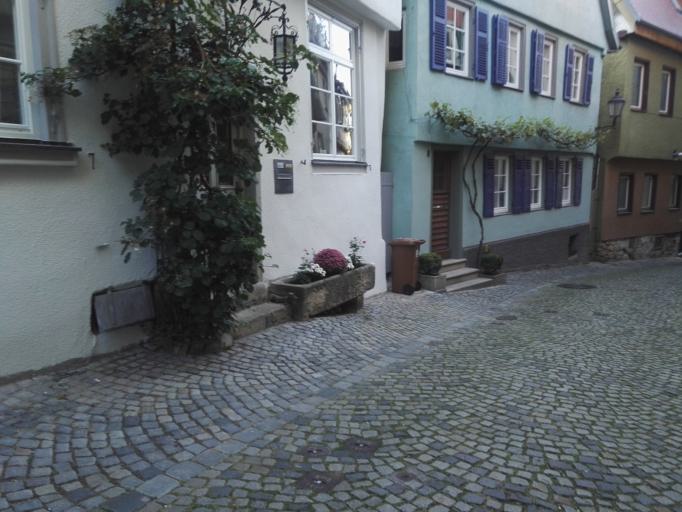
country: DE
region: Baden-Wuerttemberg
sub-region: Regierungsbezirk Stuttgart
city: Esslingen
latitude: 48.7443
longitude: 9.3067
